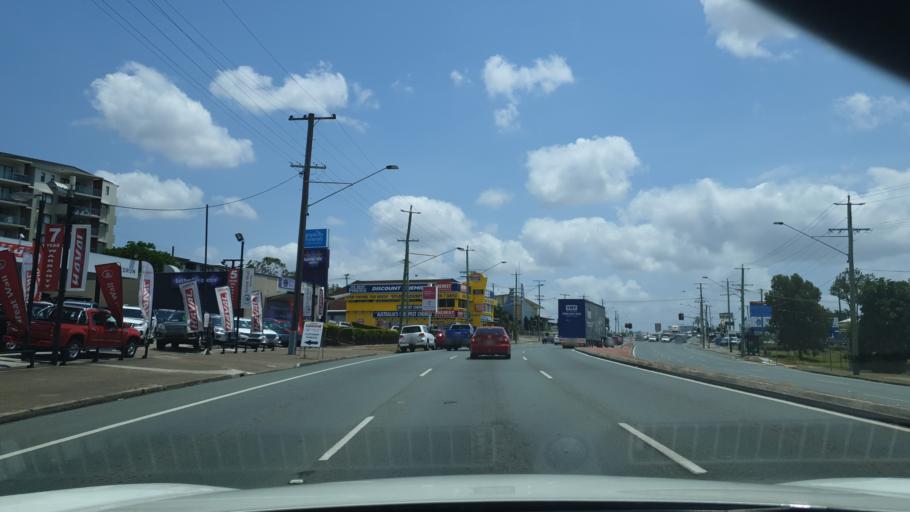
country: AU
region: Queensland
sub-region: Brisbane
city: Wavell Heights
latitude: -27.3950
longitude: 153.0308
